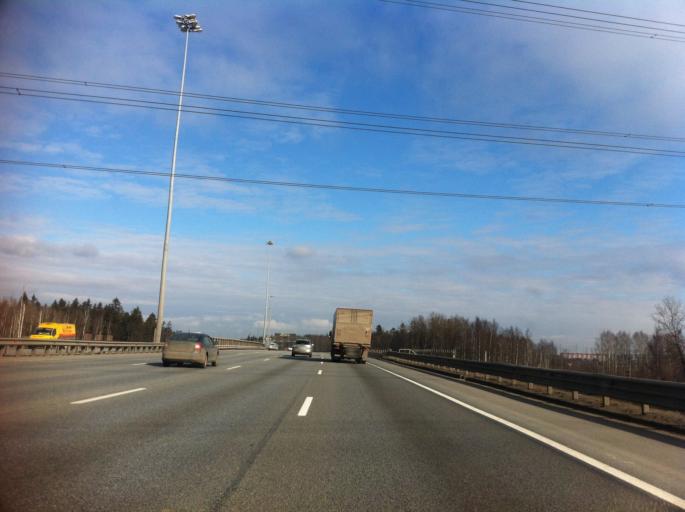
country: RU
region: St.-Petersburg
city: Krasnogvargeisky
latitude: 59.9299
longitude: 30.5359
